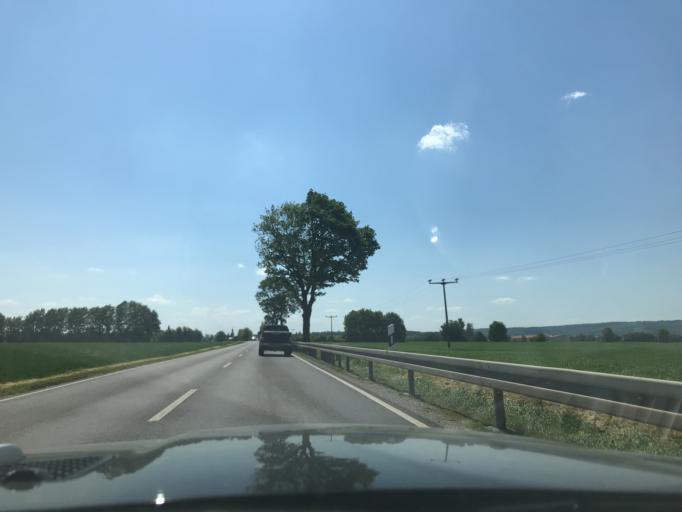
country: DE
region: Thuringia
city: Warza
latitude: 51.0066
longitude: 10.6858
